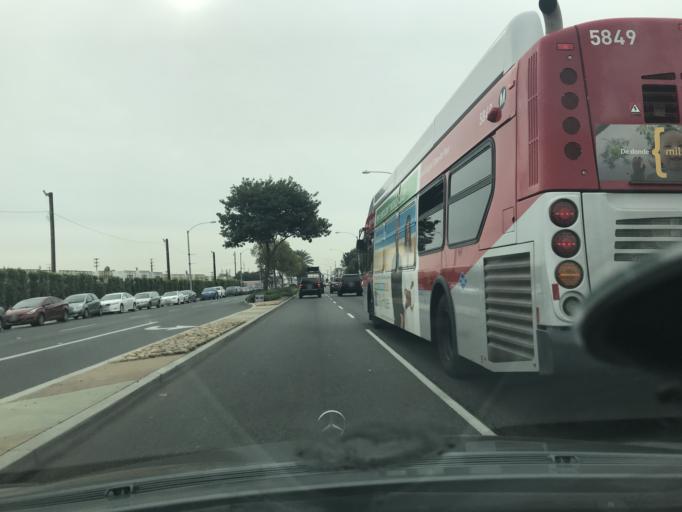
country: US
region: California
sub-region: Los Angeles County
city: Cudahy
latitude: 33.9485
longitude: -118.1819
